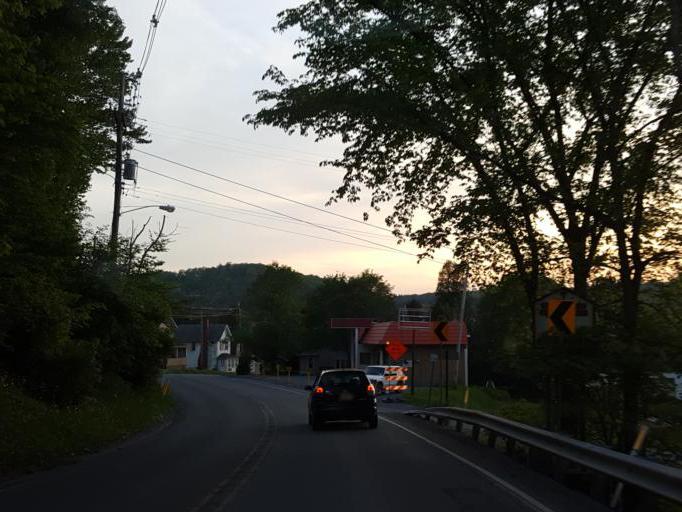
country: US
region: Pennsylvania
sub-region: Cambria County
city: Patton
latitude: 40.6343
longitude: -78.6433
